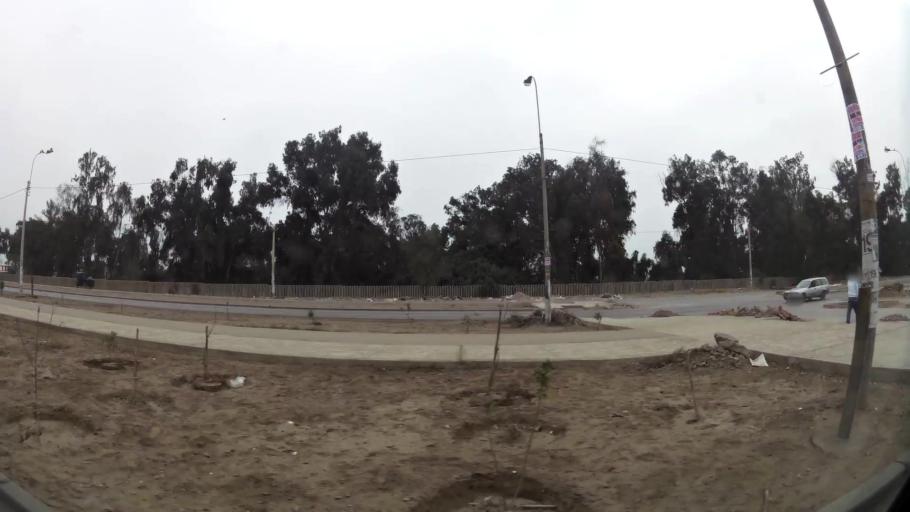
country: PE
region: Lima
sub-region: Lima
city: Surco
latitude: -12.2029
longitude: -76.9544
